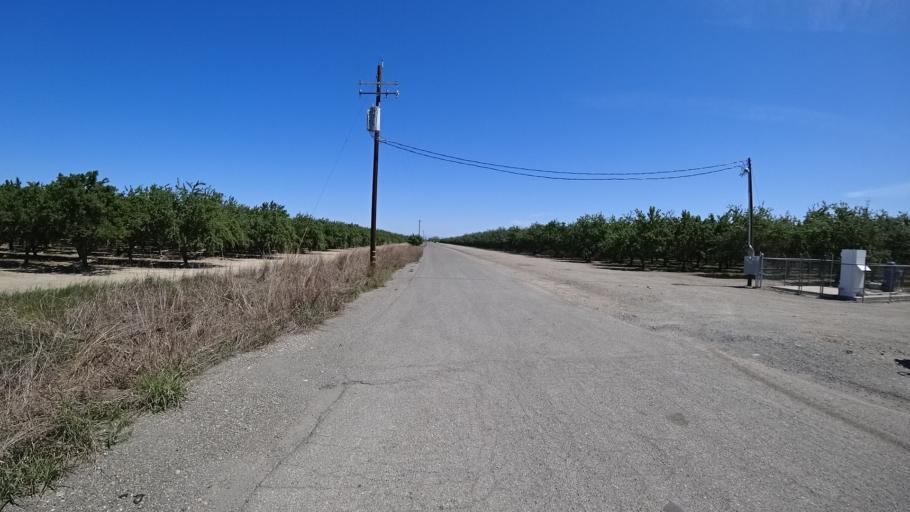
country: US
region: California
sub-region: Glenn County
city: Orland
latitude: 39.7324
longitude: -122.1408
